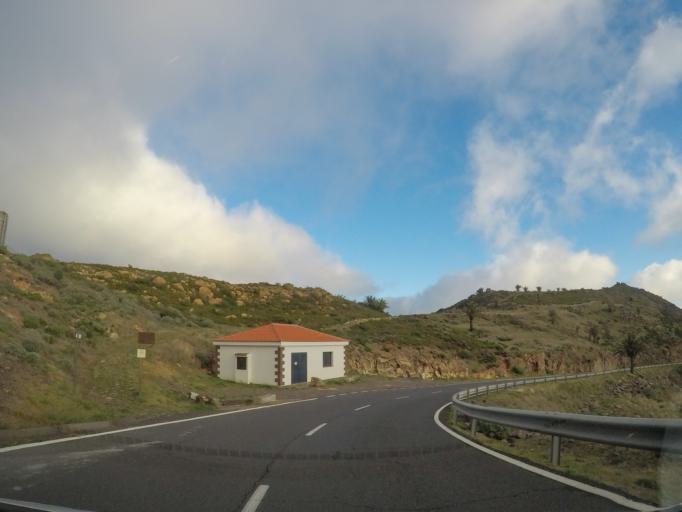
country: ES
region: Canary Islands
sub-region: Provincia de Santa Cruz de Tenerife
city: Alajero
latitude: 28.0852
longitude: -17.2456
